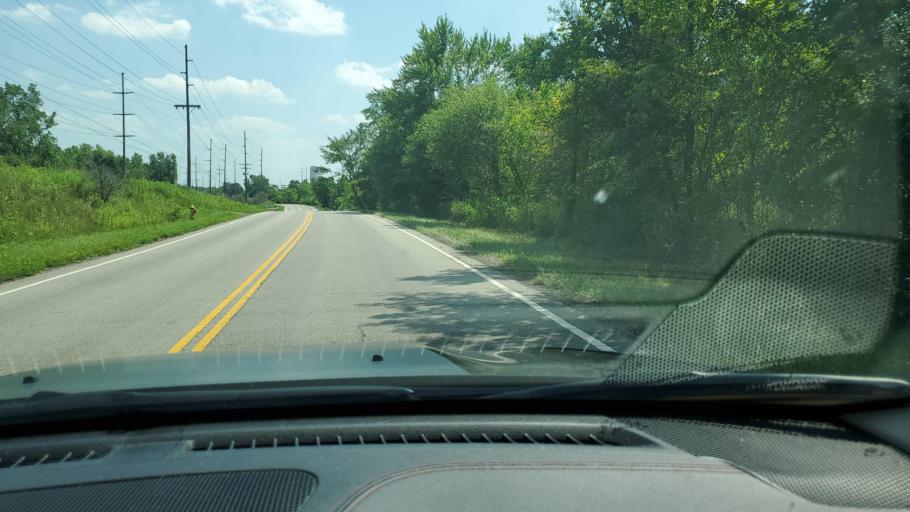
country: US
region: Ohio
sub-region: Trumbull County
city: Warren
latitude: 41.2176
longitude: -80.8064
